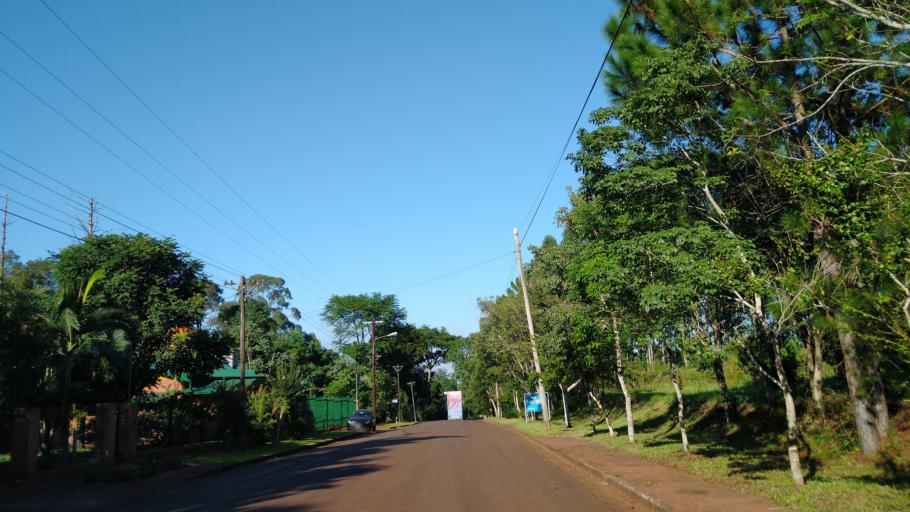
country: AR
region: Misiones
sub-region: Departamento de Montecarlo
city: Montecarlo
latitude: -26.5572
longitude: -54.7750
